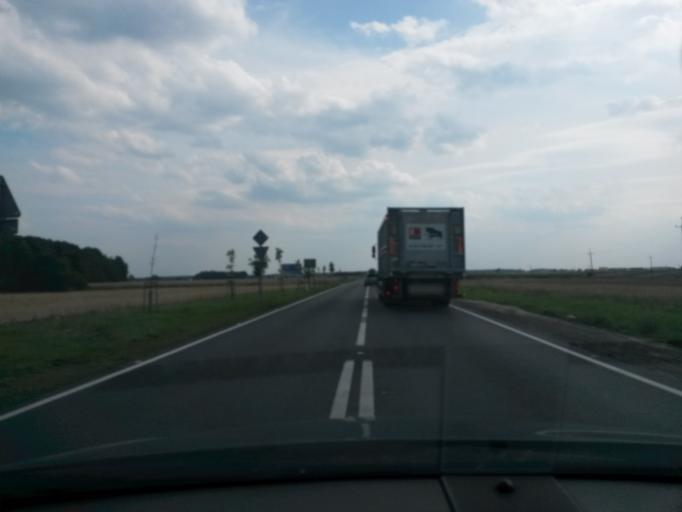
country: PL
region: Greater Poland Voivodeship
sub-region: Powiat poznanski
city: Kornik
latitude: 52.2465
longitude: 17.0541
